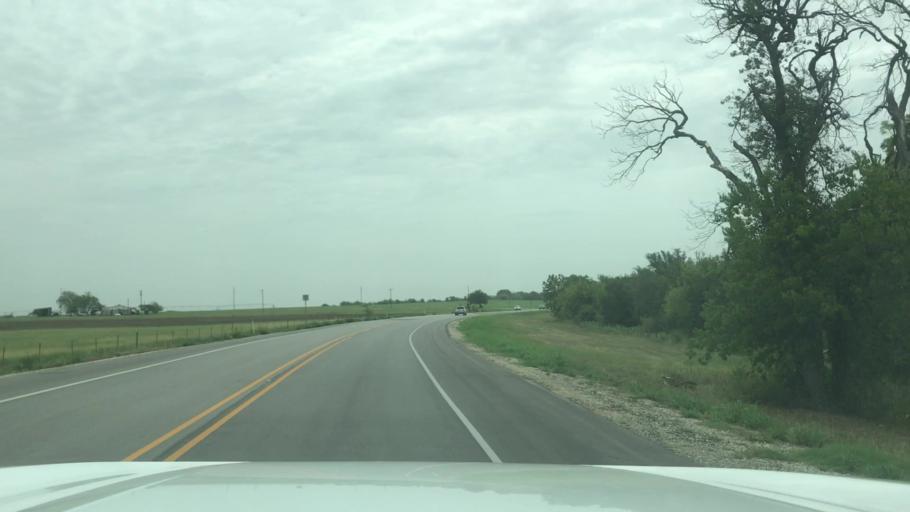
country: US
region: Texas
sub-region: Erath County
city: Dublin
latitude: 32.0917
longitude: -98.2666
